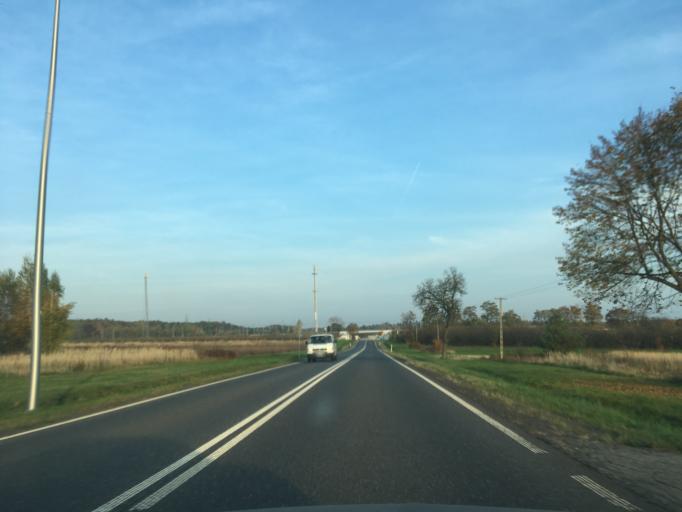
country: PL
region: Lodz Voivodeship
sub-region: Powiat skierniewicki
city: Kowiesy
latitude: 51.9204
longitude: 20.4463
